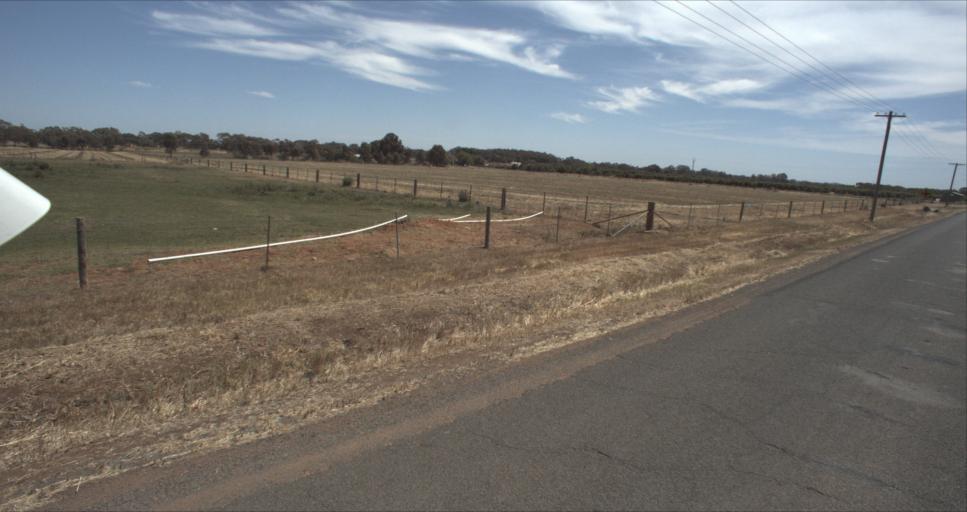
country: AU
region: New South Wales
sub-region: Leeton
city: Leeton
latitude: -34.5877
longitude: 146.4278
